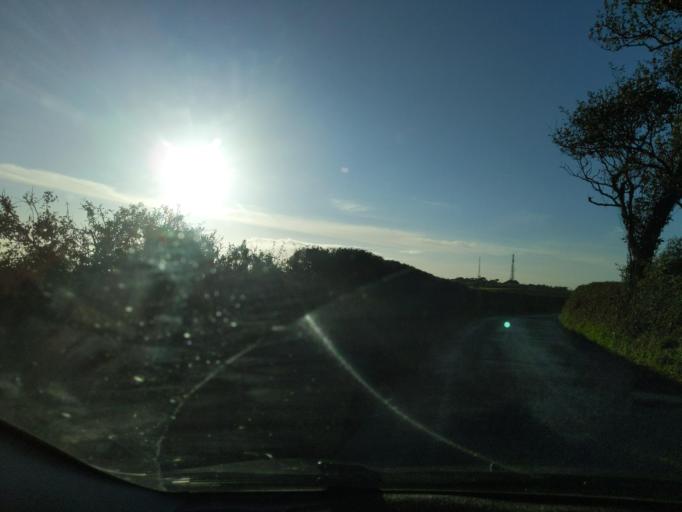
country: GB
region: England
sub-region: Plymouth
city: Plymstock
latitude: 50.3441
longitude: -4.0992
